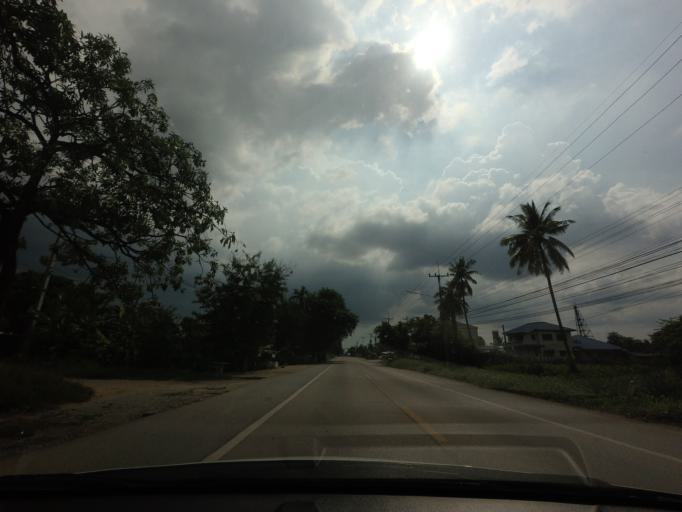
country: TH
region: Nakhon Pathom
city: Sam Phran
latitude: 13.7708
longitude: 100.2316
